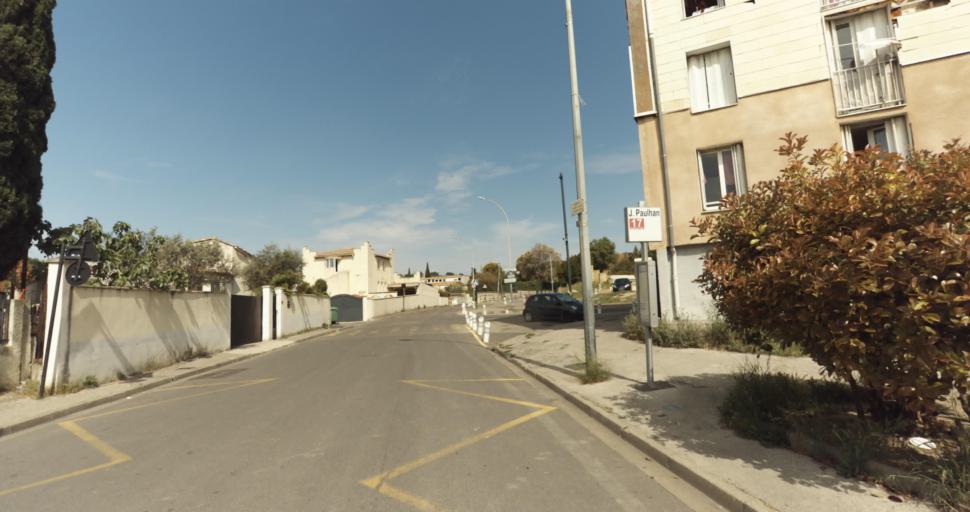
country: FR
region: Languedoc-Roussillon
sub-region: Departement du Gard
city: Rodilhan
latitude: 43.8562
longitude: 4.3973
